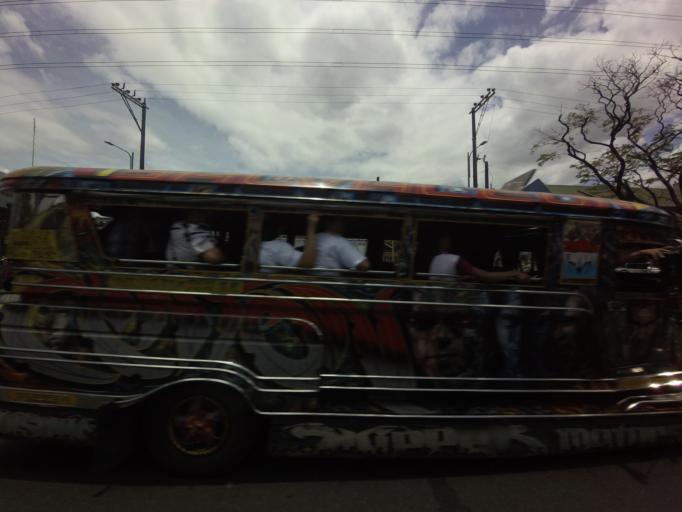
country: PH
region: Metro Manila
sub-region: Marikina
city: Calumpang
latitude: 14.6110
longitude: 121.1034
